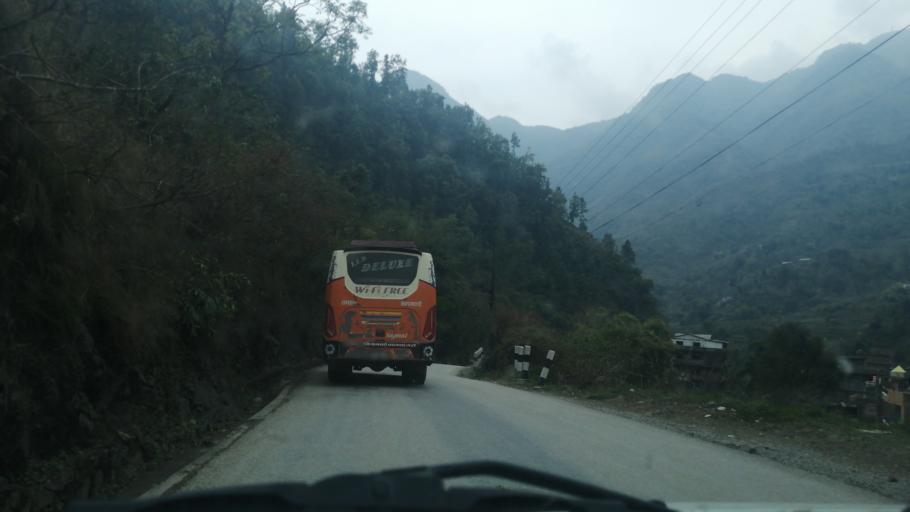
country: NP
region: Western Region
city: Tansen
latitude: 27.8044
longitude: 83.5151
